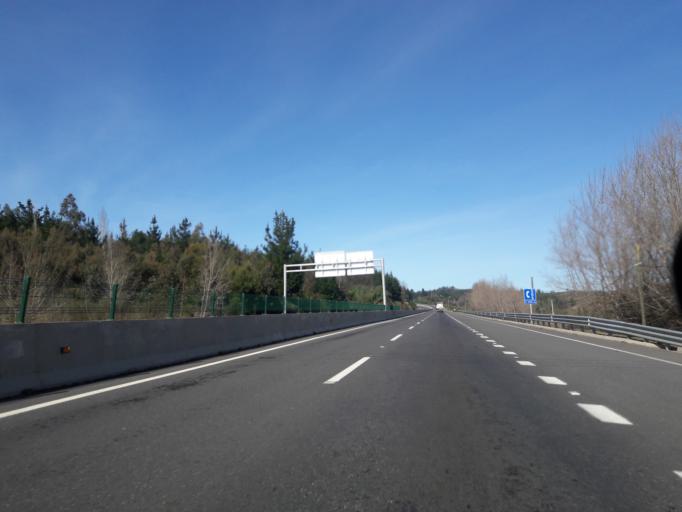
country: CL
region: Biobio
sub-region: Provincia de Concepcion
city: Chiguayante
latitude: -36.9179
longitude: -72.7749
